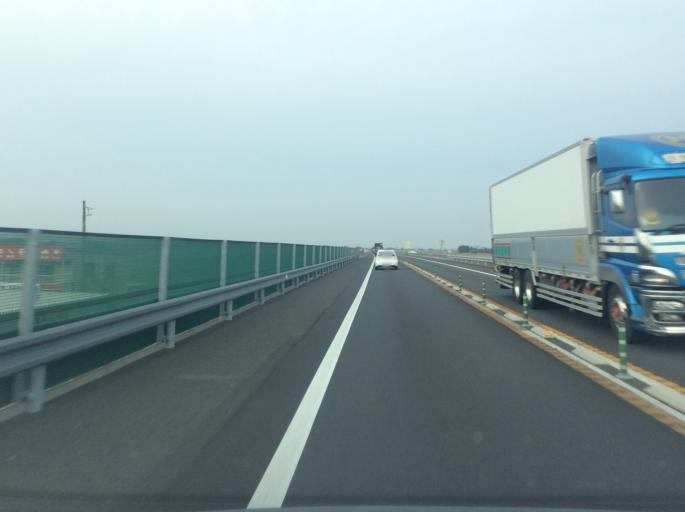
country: JP
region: Miyagi
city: Watari
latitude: 38.0555
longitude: 140.8938
